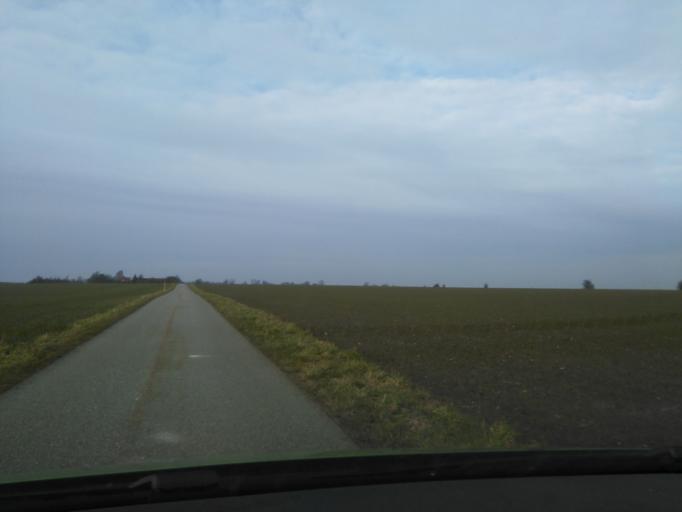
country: DK
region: Central Jutland
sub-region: Odder Kommune
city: Odder
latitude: 55.8926
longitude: 10.1323
